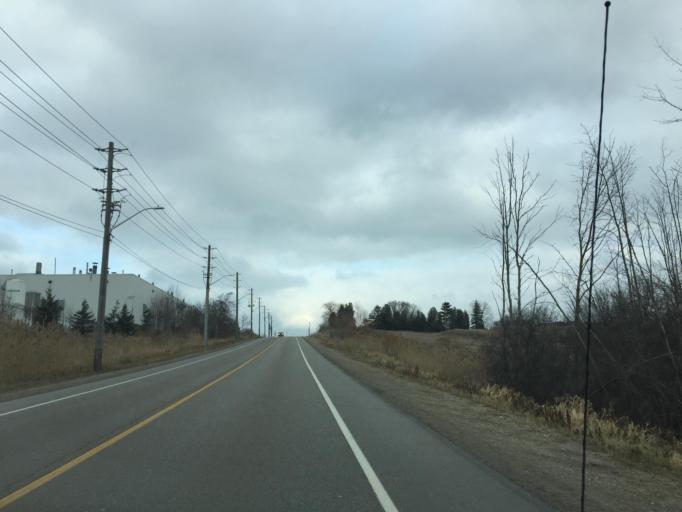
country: CA
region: Ontario
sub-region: Wellington County
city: Guelph
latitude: 43.5290
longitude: -80.3086
